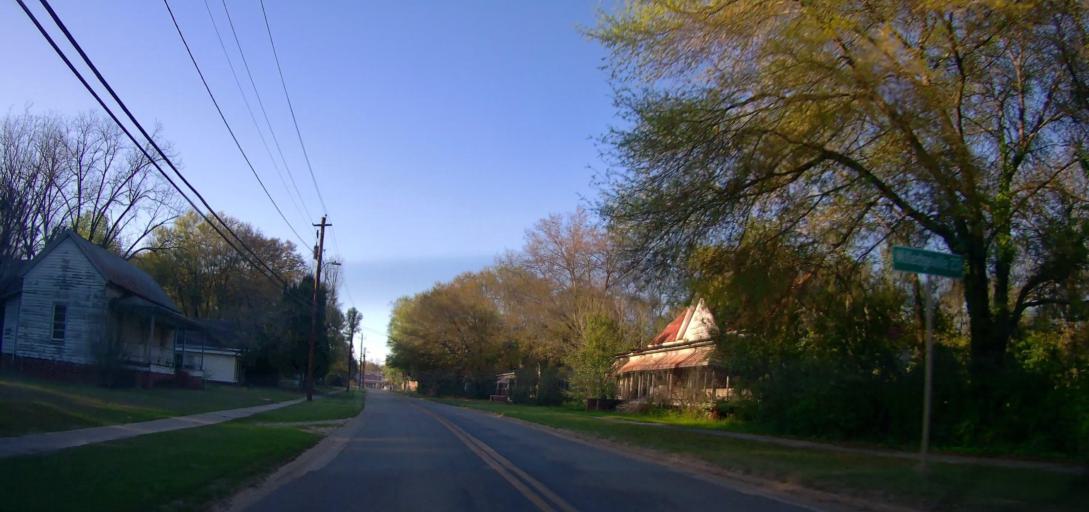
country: US
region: Georgia
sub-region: Wilkinson County
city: Irwinton
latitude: 32.8233
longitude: -83.0788
